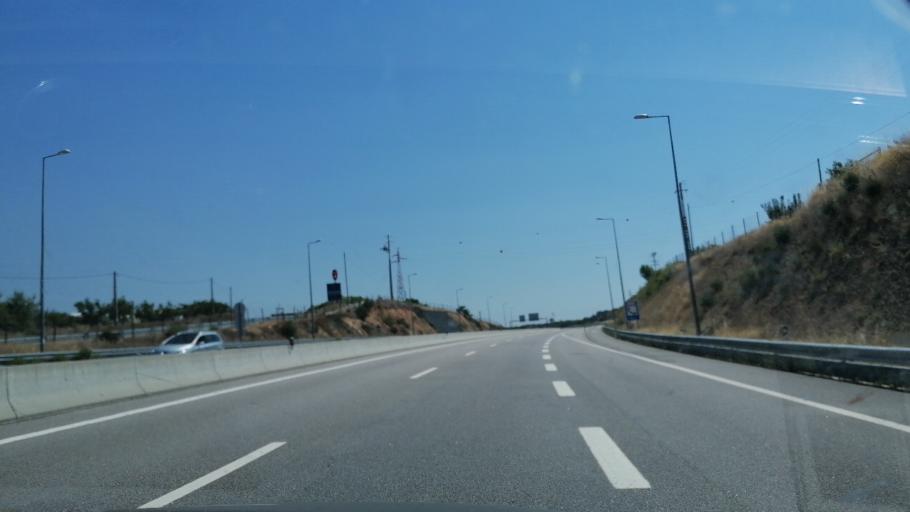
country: PT
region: Braganca
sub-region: Macedo de Cavaleiros
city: Macedo de Cavaleiros
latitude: 41.5826
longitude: -6.9388
